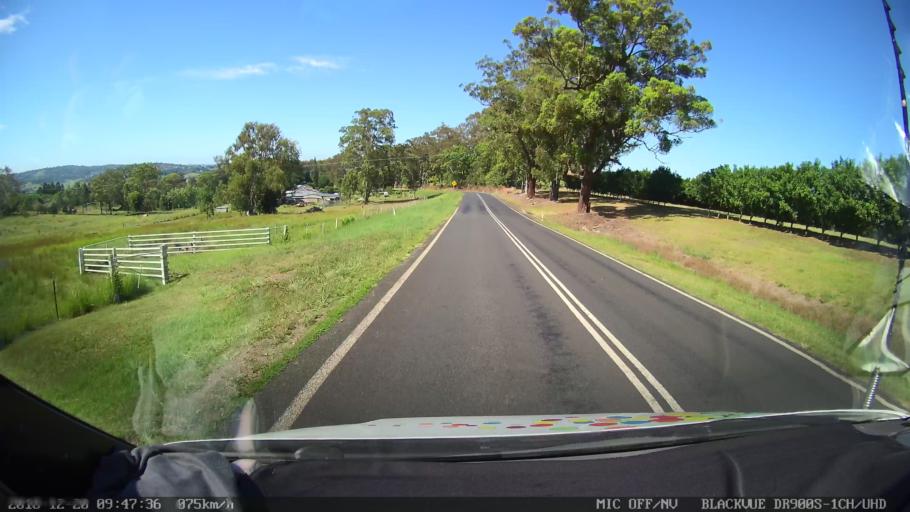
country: AU
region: New South Wales
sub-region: Lismore Municipality
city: Lismore
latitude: -28.7646
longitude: 153.2960
